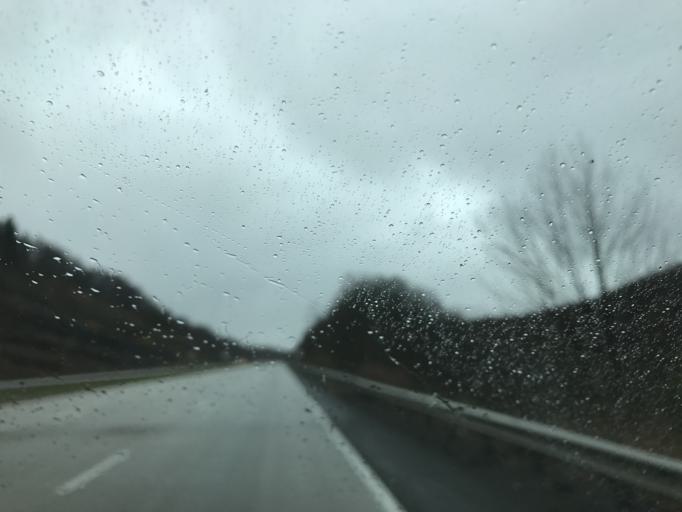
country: US
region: West Virginia
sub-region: Greenbrier County
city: Rainelle
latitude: 37.8336
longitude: -80.7713
